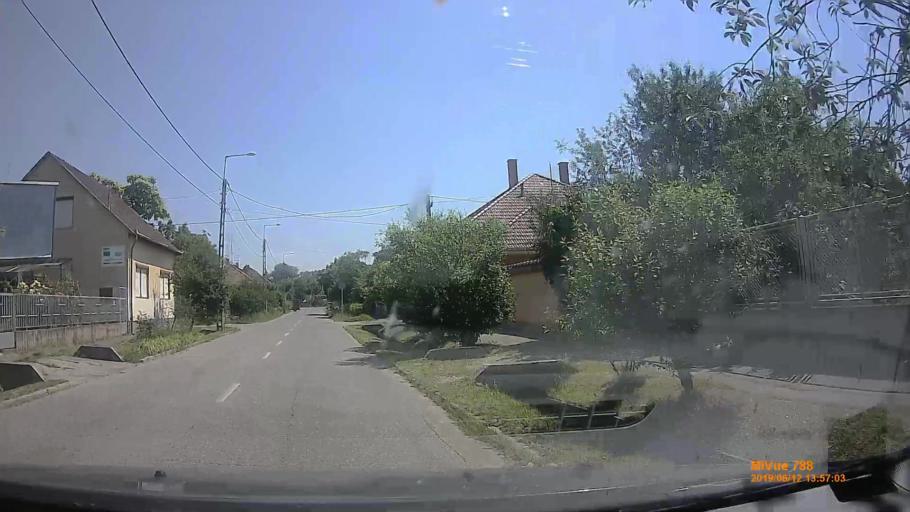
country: HU
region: Csongrad
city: Szeged
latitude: 46.2605
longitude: 20.1814
